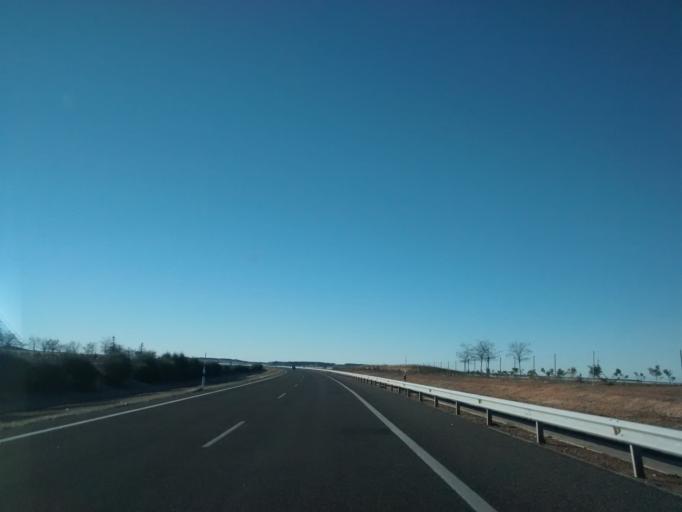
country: ES
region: Castille and Leon
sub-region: Provincia de Palencia
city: Pradanos de Ojeda
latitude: 42.6567
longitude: -4.3470
